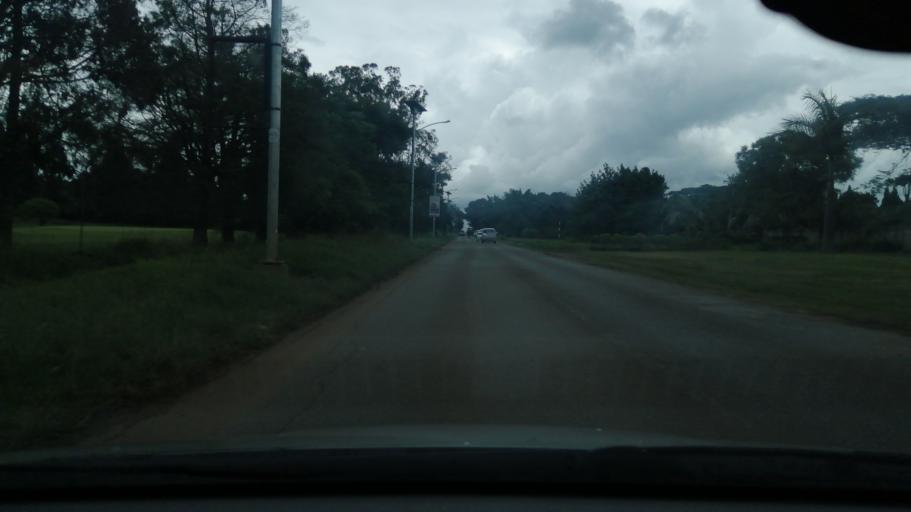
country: ZW
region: Harare
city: Harare
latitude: -17.7996
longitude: 31.0732
